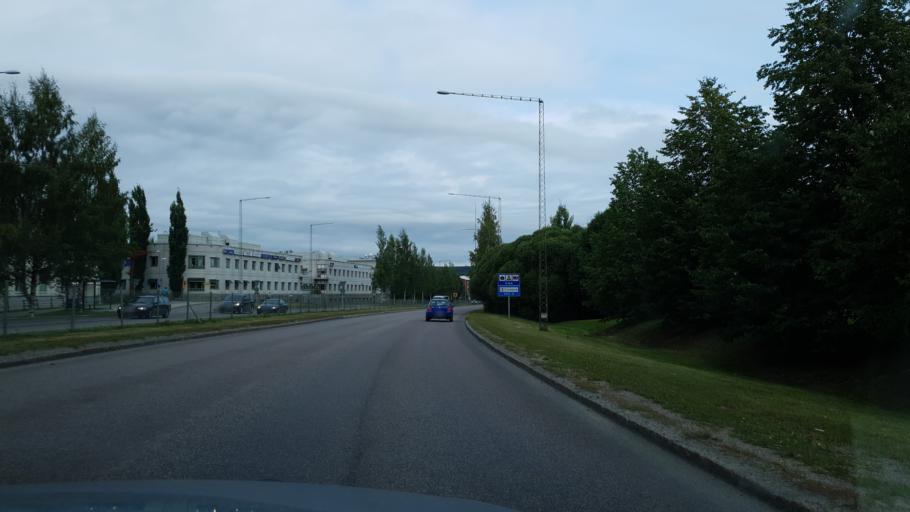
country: SE
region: Vaesterbotten
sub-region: Skelleftea Kommun
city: Skelleftea
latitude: 64.7442
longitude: 20.9602
